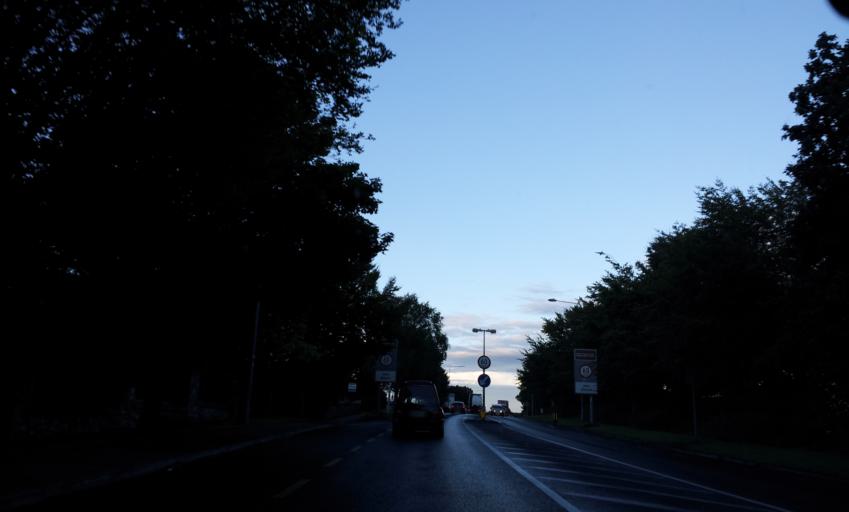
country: IE
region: Munster
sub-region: County Limerick
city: Newcastle West
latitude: 52.4513
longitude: -9.0464
